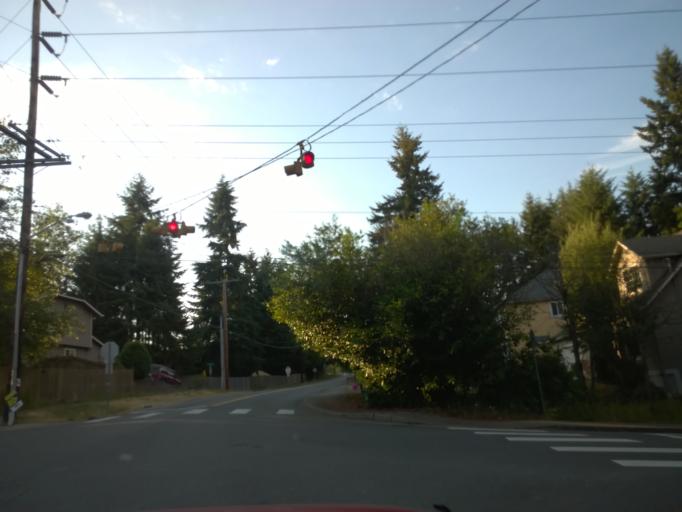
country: US
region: Washington
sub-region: King County
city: Woodinville
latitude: 47.7694
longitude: -122.1665
